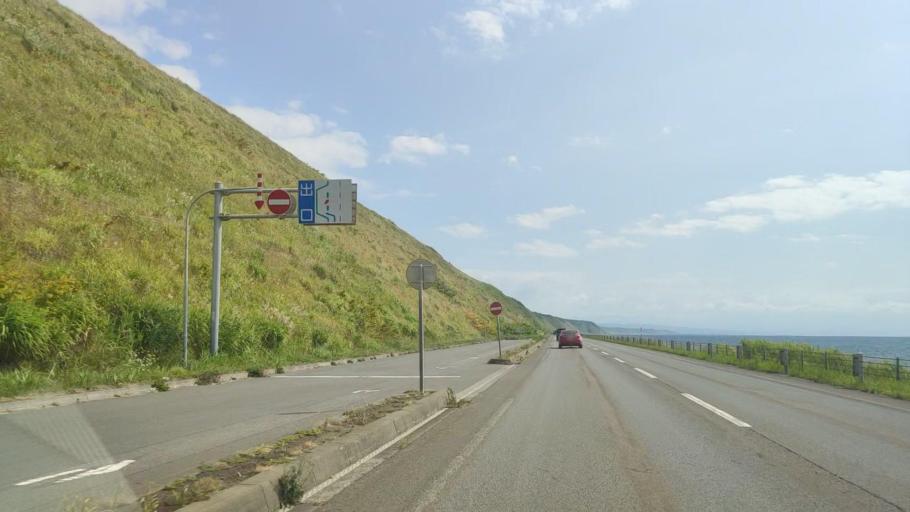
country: JP
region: Hokkaido
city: Rumoi
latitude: 44.0684
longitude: 141.6629
